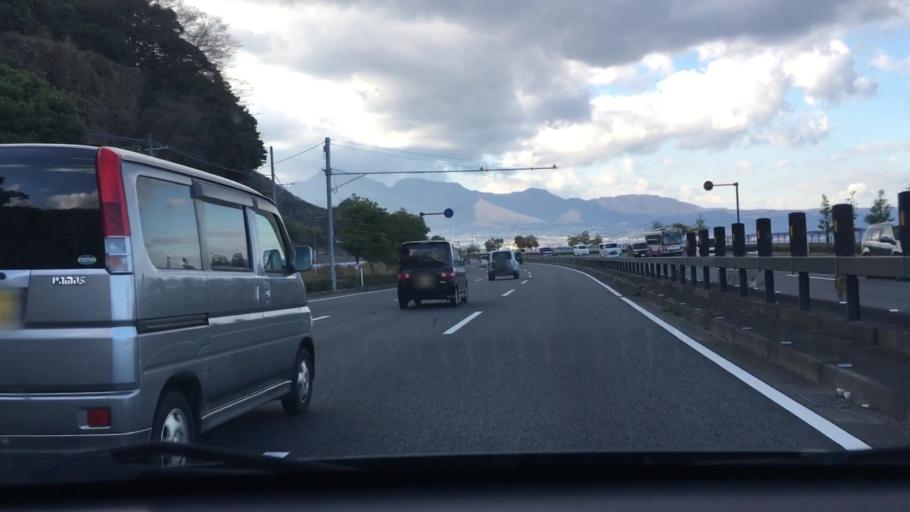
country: JP
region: Oita
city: Oita
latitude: 33.2514
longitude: 131.5698
